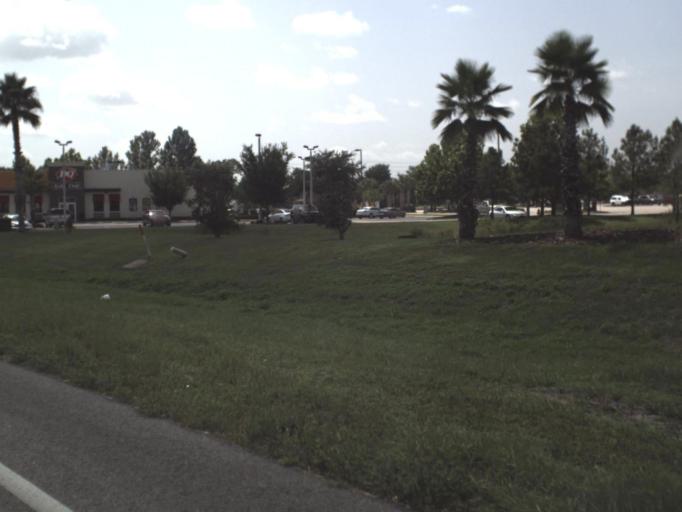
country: US
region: Florida
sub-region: Highlands County
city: Sebring
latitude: 27.5045
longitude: -81.4915
